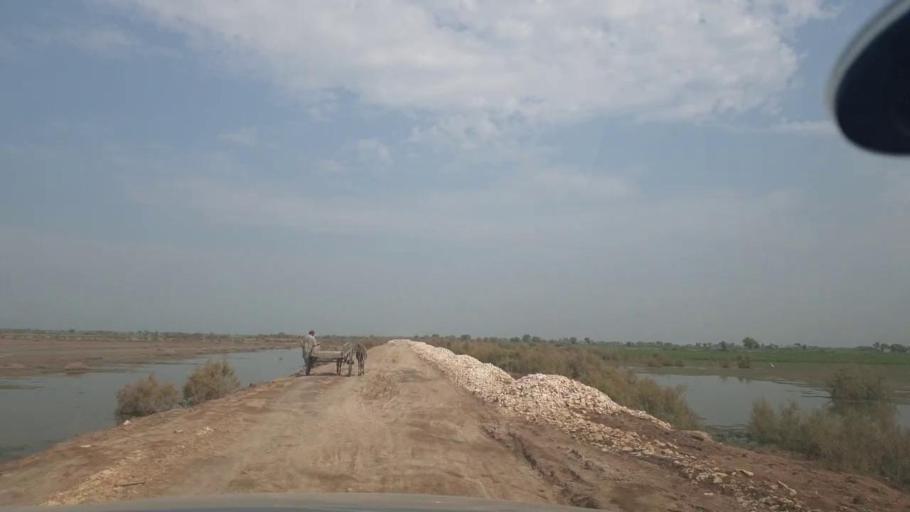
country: PK
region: Balochistan
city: Mehrabpur
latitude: 28.0837
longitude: 68.0992
